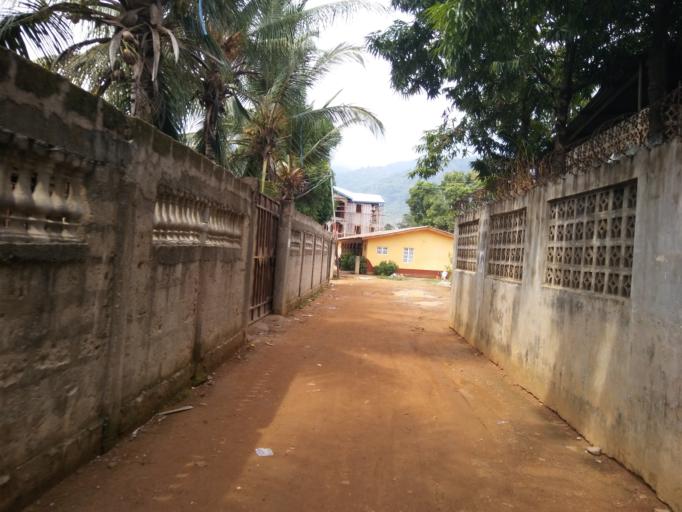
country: SL
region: Western Area
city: Hastings
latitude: 8.3847
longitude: -13.1492
